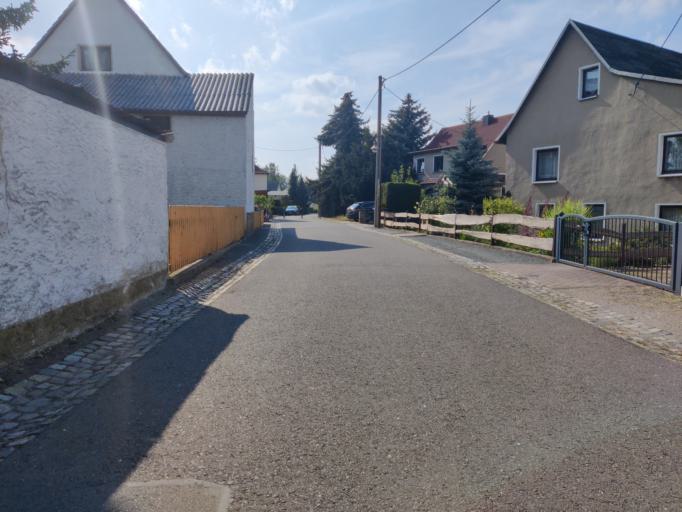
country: DE
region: Thuringia
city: Fockendorf
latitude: 51.0516
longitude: 12.4524
